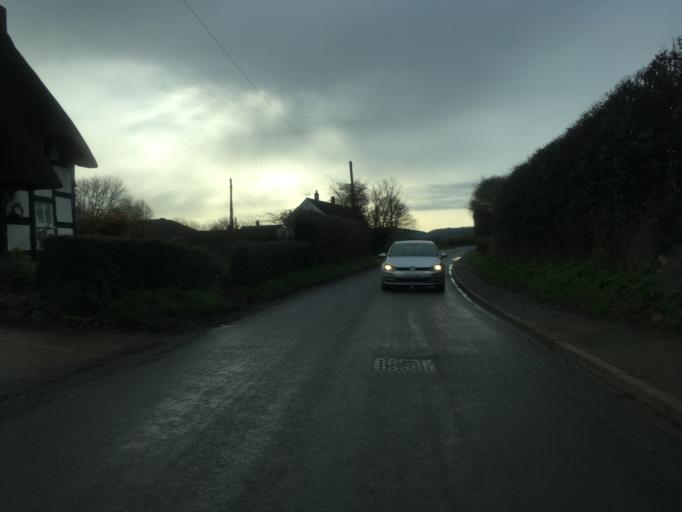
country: GB
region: England
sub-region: Worcestershire
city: Evesham
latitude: 52.0352
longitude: -2.0065
